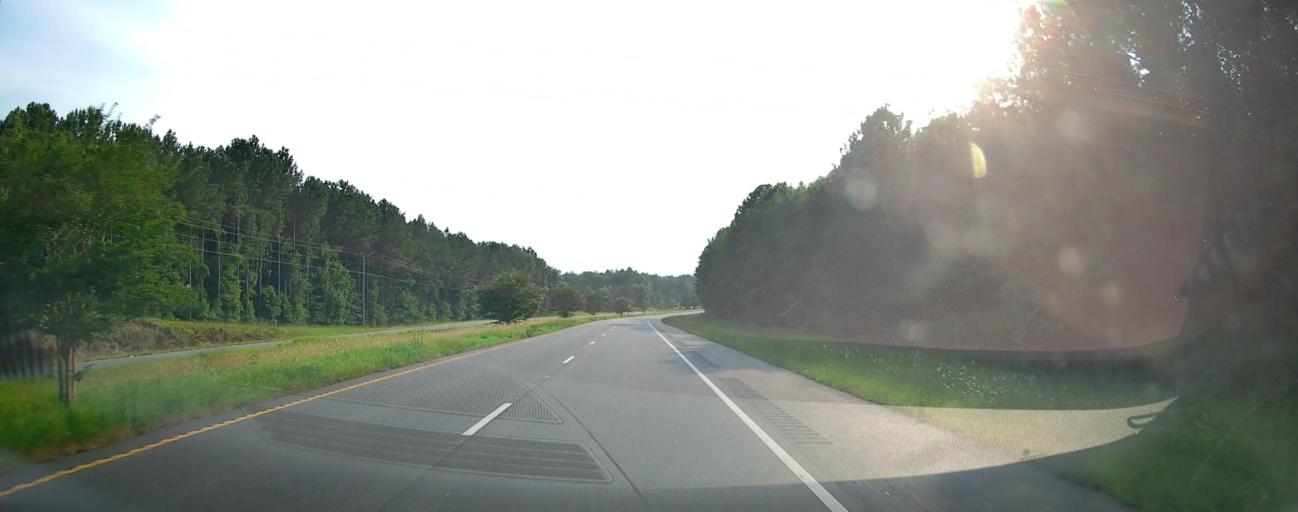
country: US
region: Georgia
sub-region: Talbot County
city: Talbotton
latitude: 32.5465
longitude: -84.7103
